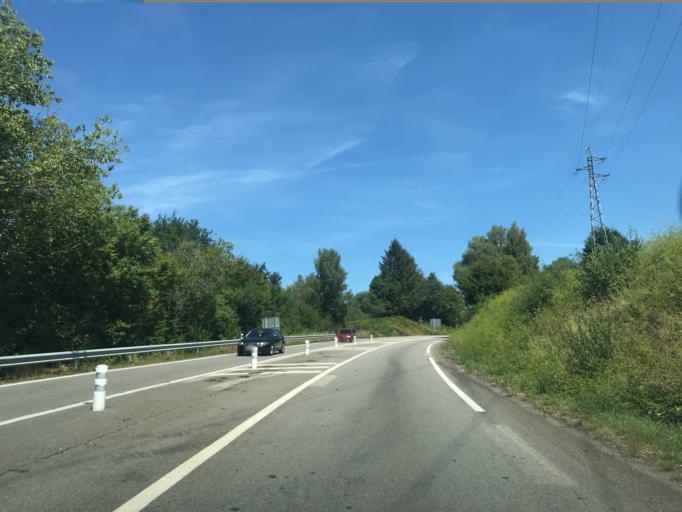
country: FR
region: Limousin
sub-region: Departement de la Correze
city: Tulle
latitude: 45.2845
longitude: 1.7984
